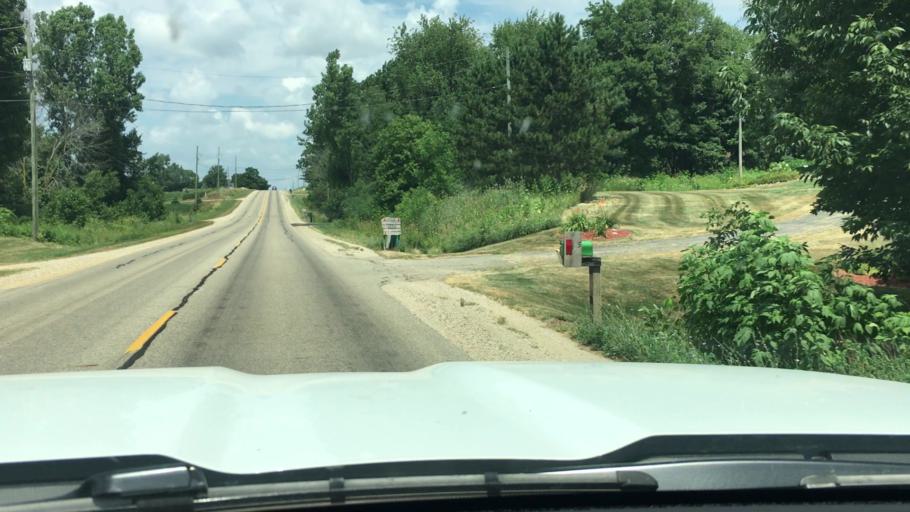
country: US
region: Michigan
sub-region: Ottawa County
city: Hudsonville
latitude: 42.8031
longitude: -85.8419
